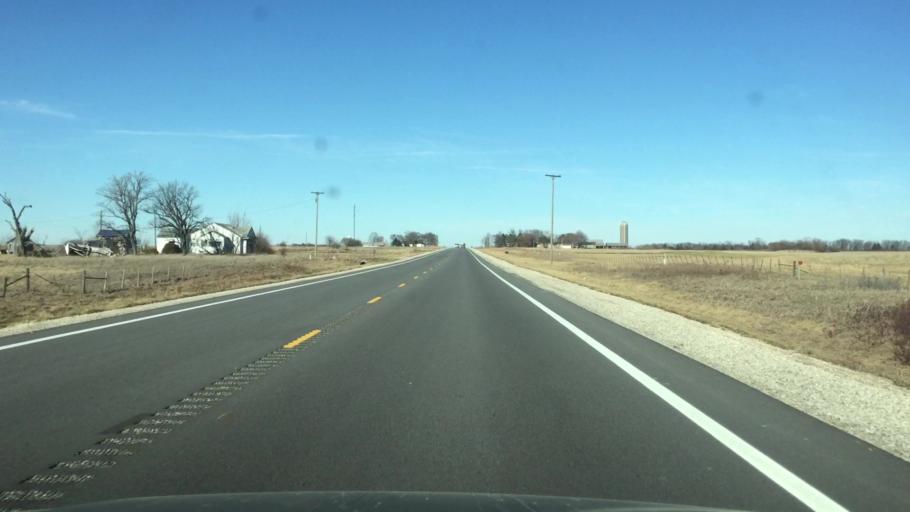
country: US
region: Kansas
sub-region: Anderson County
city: Garnett
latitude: 38.3775
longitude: -95.2488
